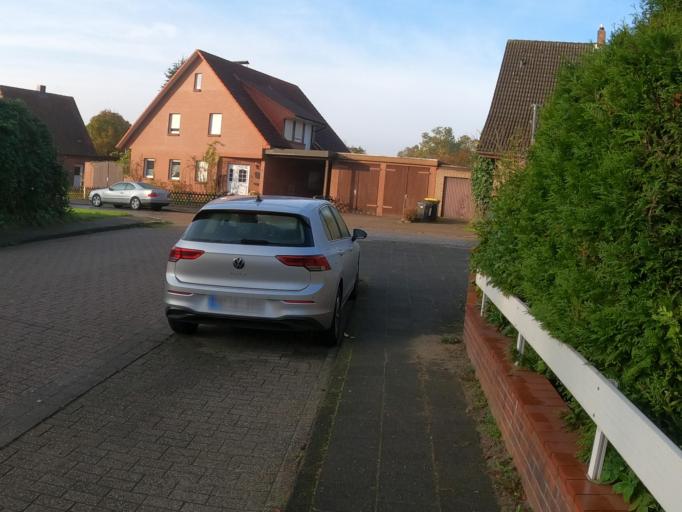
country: DE
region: Lower Saxony
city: Stade
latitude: 53.6084
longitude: 9.4621
